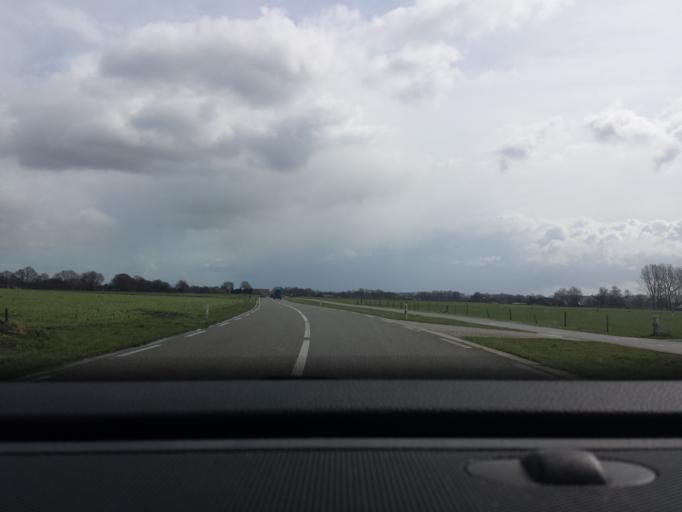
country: NL
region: Gelderland
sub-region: Gemeente Bronckhorst
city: Zelhem
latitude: 51.9989
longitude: 6.4073
